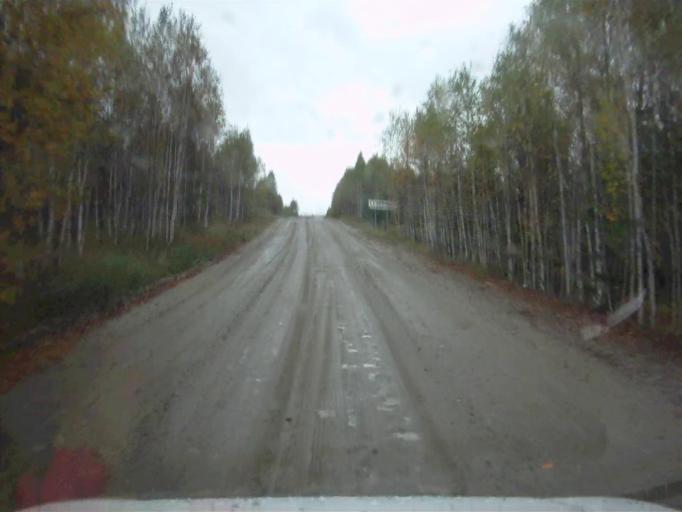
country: RU
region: Chelyabinsk
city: Kyshtym
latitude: 55.8462
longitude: 60.4855
